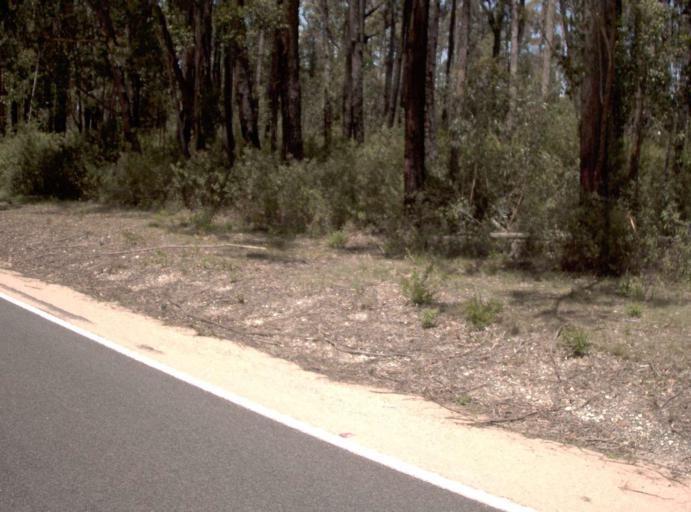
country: AU
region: Victoria
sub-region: East Gippsland
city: Lakes Entrance
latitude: -37.6857
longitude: 148.7620
